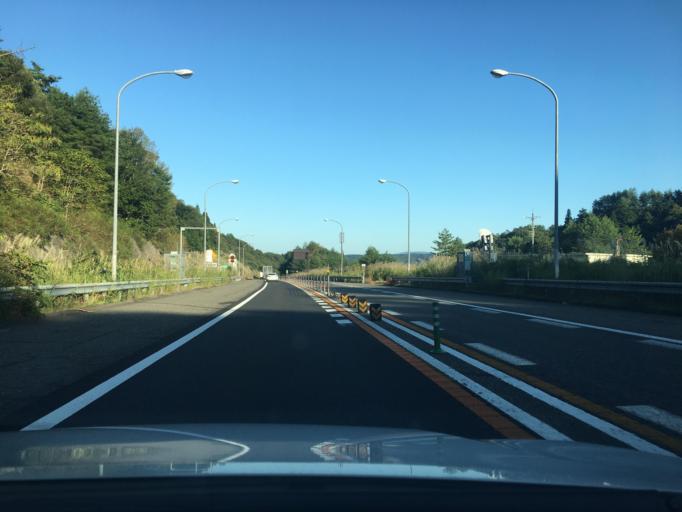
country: JP
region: Fukushima
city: Kitakata
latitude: 37.5695
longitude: 139.7295
